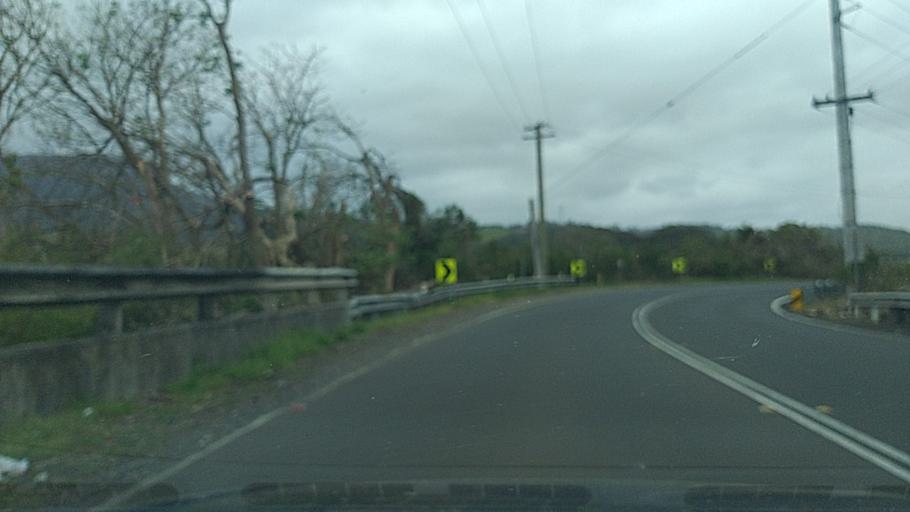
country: AU
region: New South Wales
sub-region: Wollongong
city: Dapto
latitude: -34.4694
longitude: 150.7959
